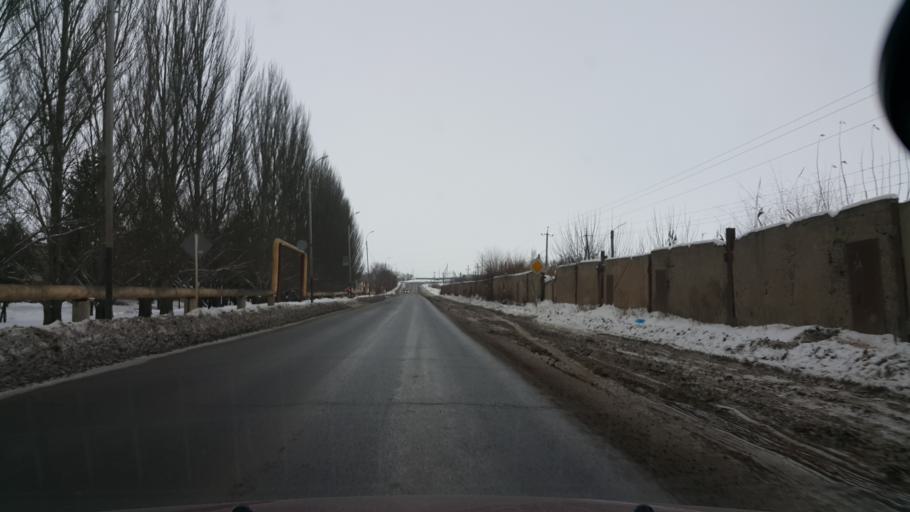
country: RU
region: Tambov
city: Pokrovo-Prigorodnoye
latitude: 52.6601
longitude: 41.4156
